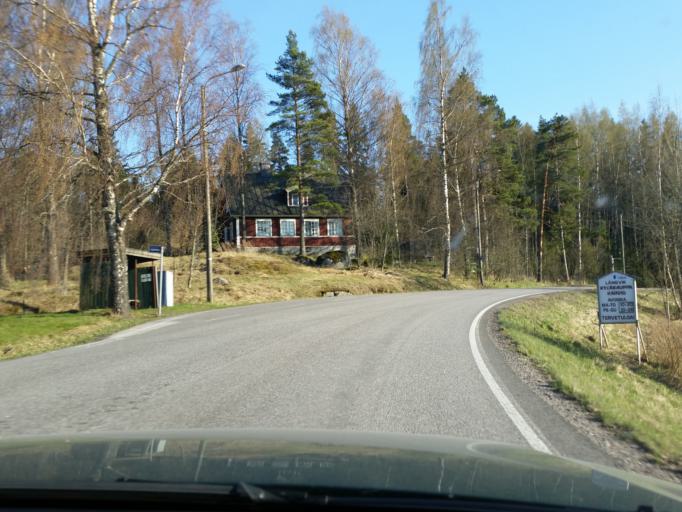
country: FI
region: Uusimaa
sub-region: Helsinki
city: Espoo
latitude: 60.1100
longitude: 24.5695
